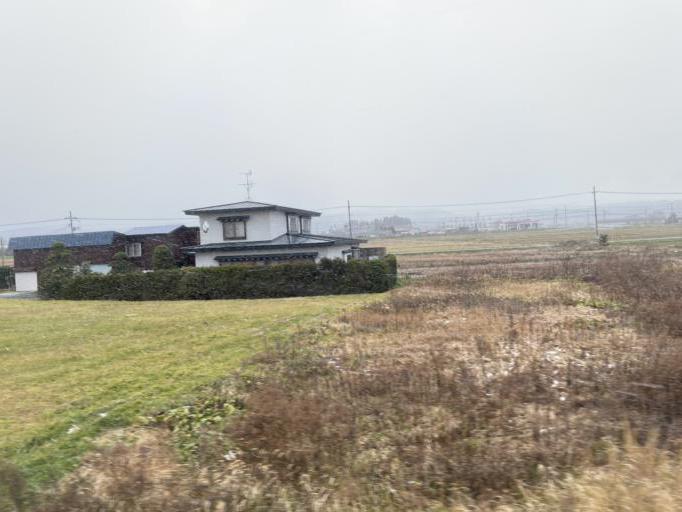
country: JP
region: Aomori
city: Aomori Shi
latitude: 40.9713
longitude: 140.6546
